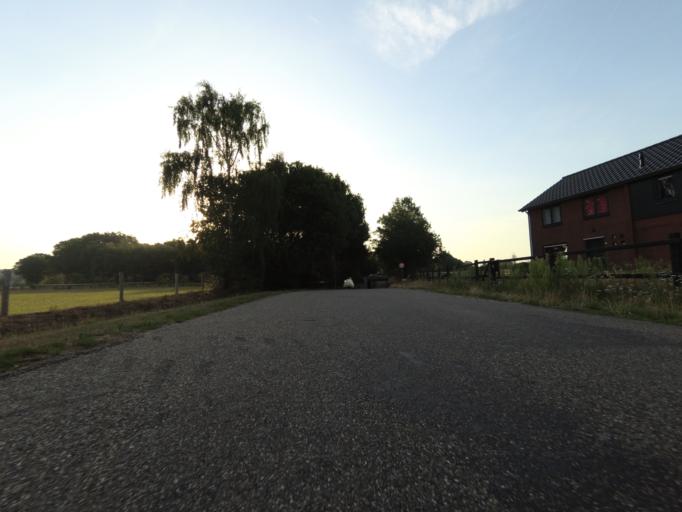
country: NL
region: Gelderland
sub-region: Gemeente Lochem
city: Laren
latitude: 52.2864
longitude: 6.3966
